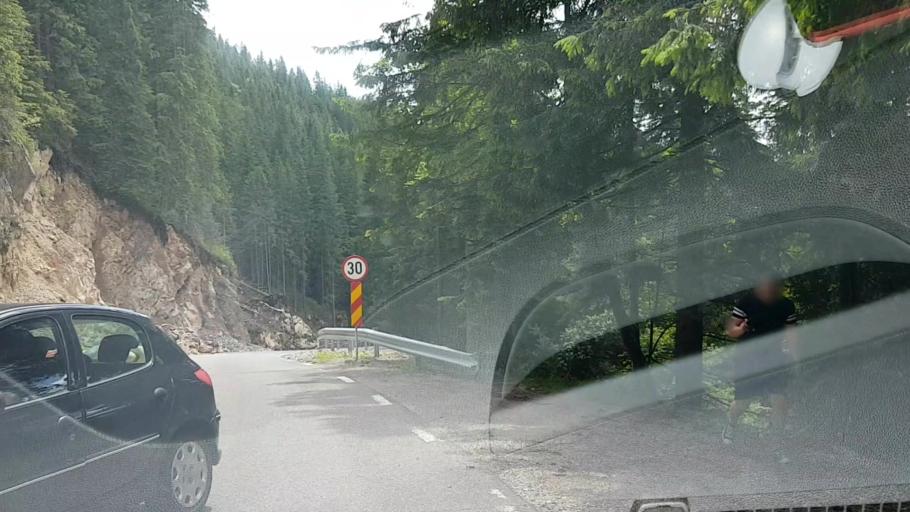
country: RO
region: Suceava
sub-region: Municipiul Campulung Moldovenesc
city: Campulung Moldovenesc
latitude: 47.4468
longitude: 25.5551
